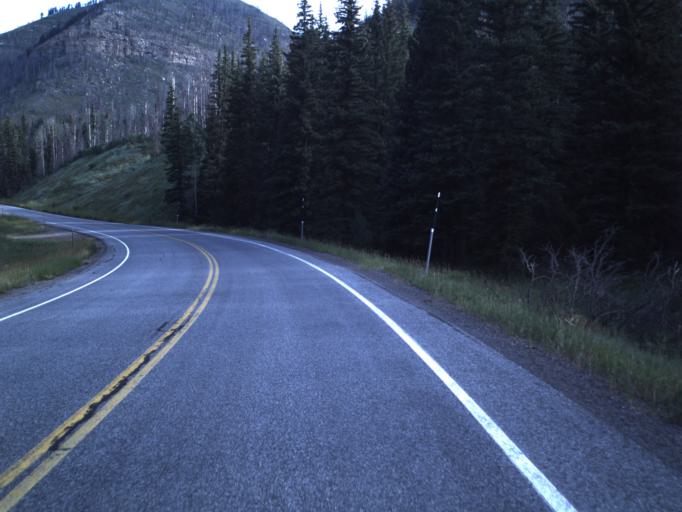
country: US
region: Utah
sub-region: Emery County
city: Huntington
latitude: 39.5312
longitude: -111.1550
